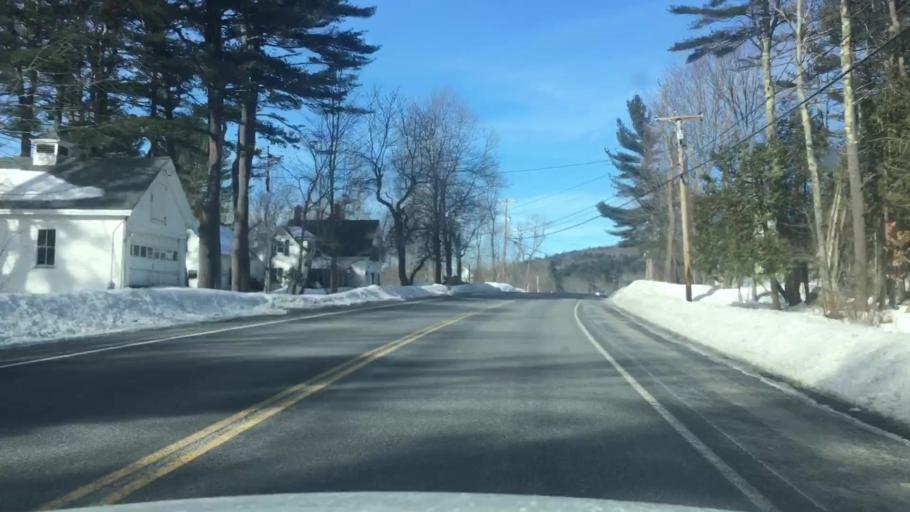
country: US
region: Maine
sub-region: Penobscot County
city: Orrington
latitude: 44.6867
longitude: -68.8109
